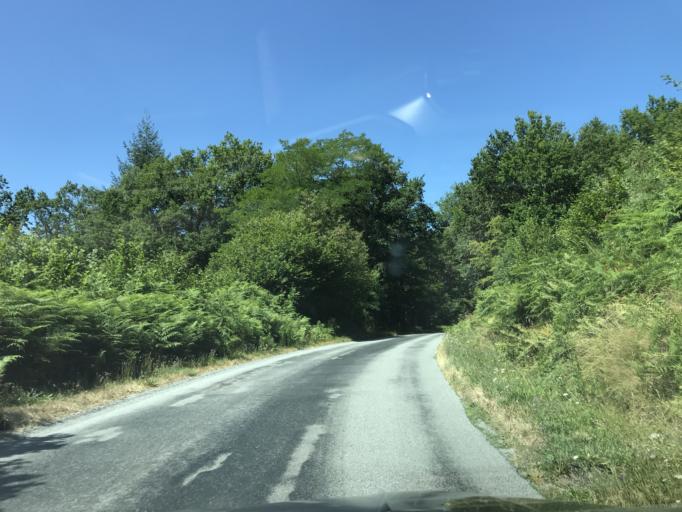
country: FR
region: Limousin
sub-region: Departement de la Correze
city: Neuvic
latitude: 45.3745
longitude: 2.2358
